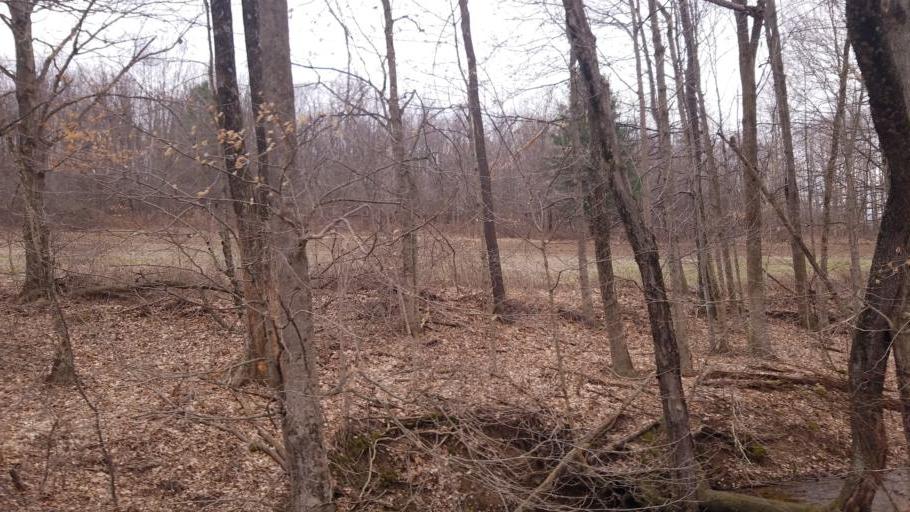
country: US
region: Ohio
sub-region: Sandusky County
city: Bellville
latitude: 40.5727
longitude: -82.4021
